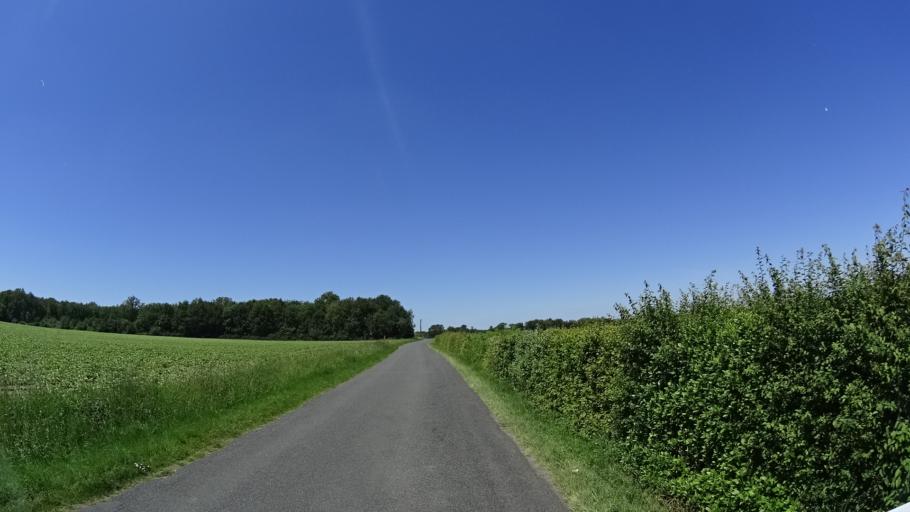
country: FR
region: Pays de la Loire
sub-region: Departement de Maine-et-Loire
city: Chenehutte-Treves-Cunault
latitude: 47.2870
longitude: -0.1426
